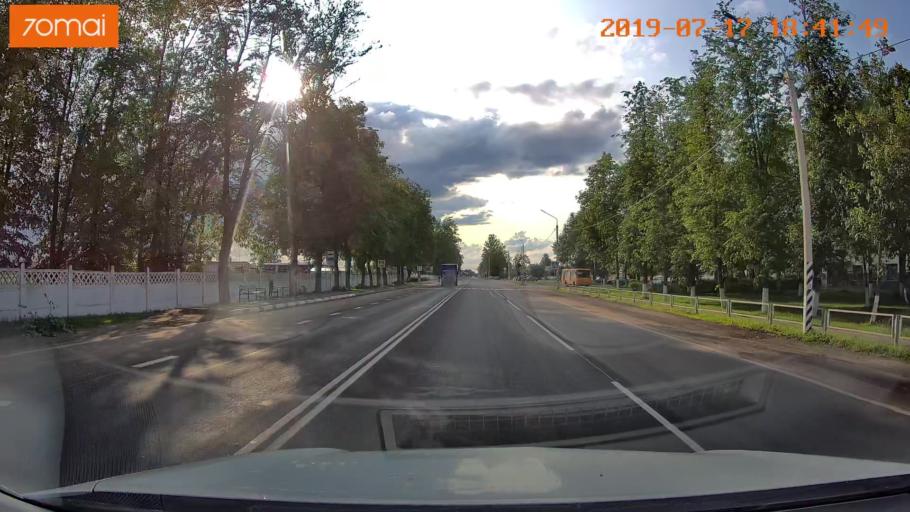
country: BY
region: Mogilev
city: Asipovichy
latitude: 53.3074
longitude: 28.6565
